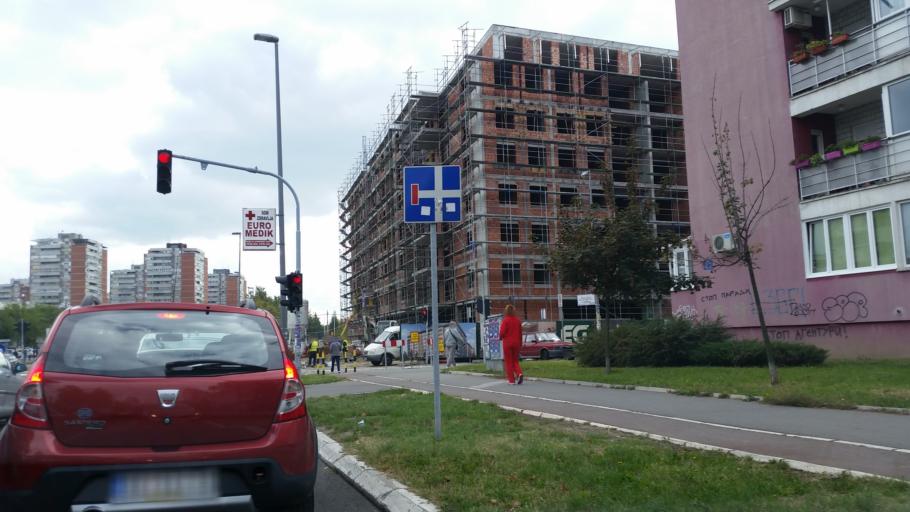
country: RS
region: Central Serbia
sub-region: Belgrade
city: Novi Beograd
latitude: 44.8047
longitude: 20.3871
